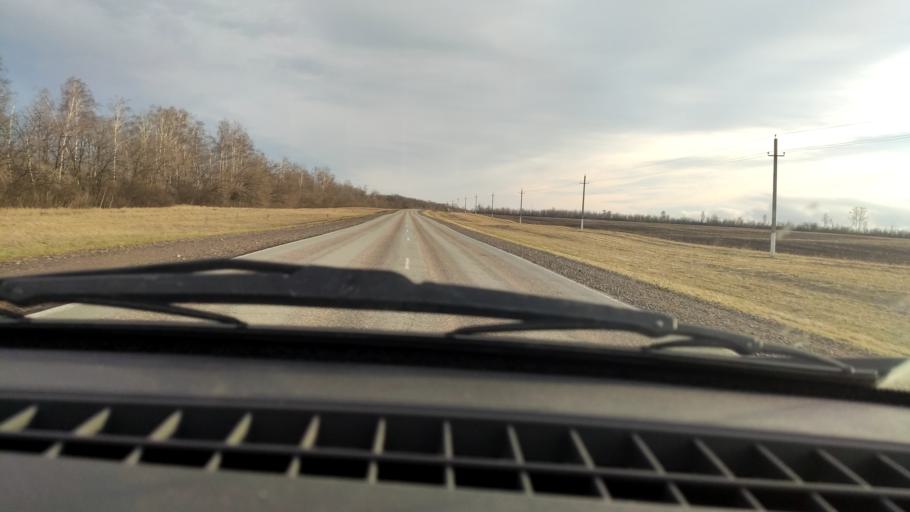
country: RU
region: Bashkortostan
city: Davlekanovo
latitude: 54.3332
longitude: 55.1677
